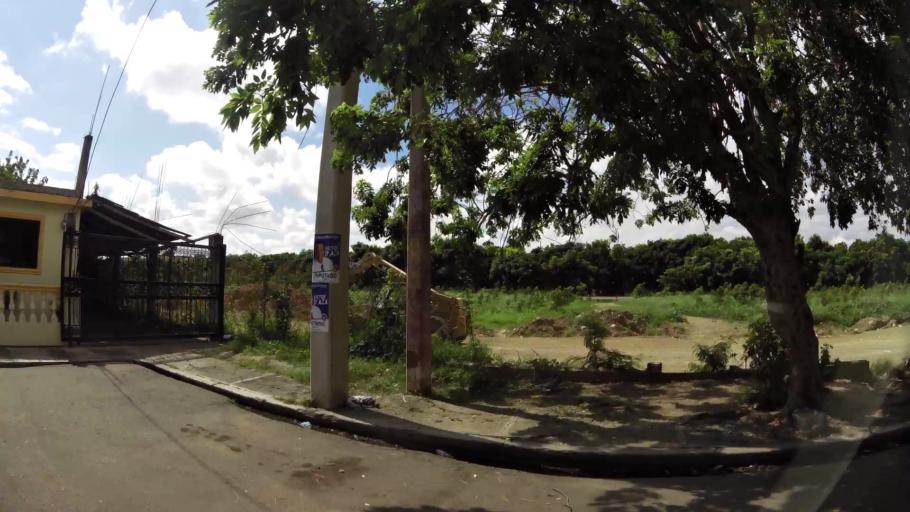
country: DO
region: Santiago
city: Santiago de los Caballeros
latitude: 19.4696
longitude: -70.6977
